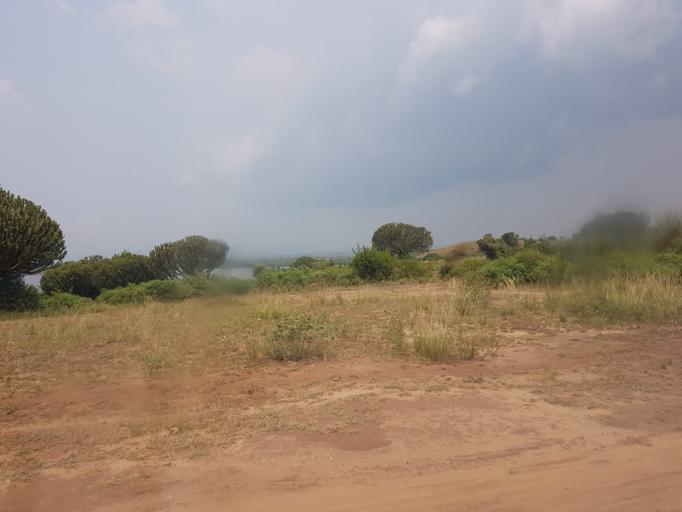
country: UG
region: Western Region
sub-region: Rubirizi District
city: Rubirizi
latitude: -0.0770
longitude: 30.1733
